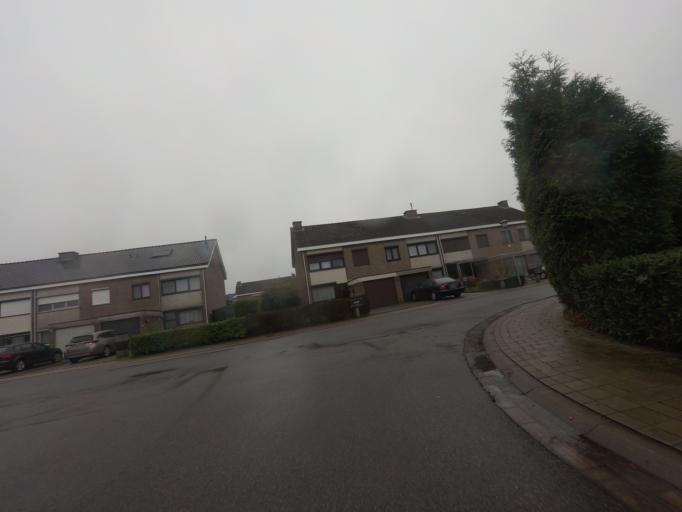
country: BE
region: Flanders
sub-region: Provincie Antwerpen
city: Hoboken
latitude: 51.1836
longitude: 4.3421
